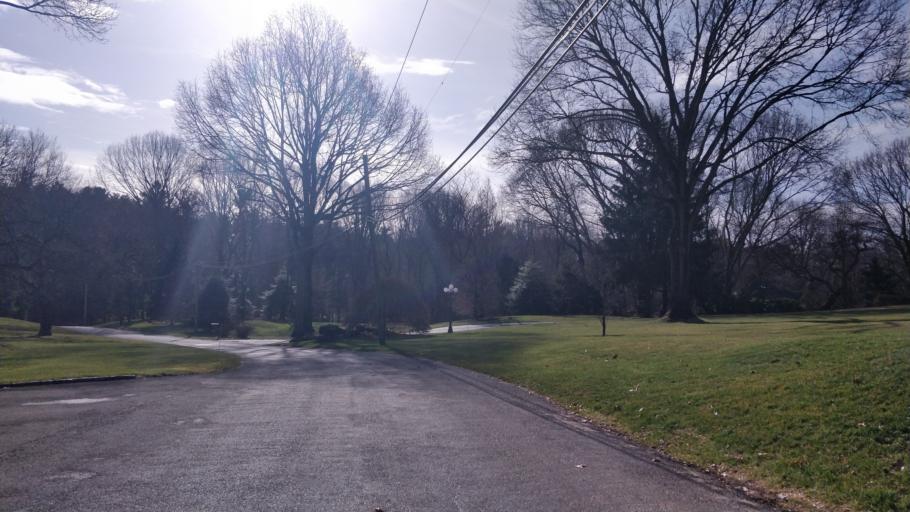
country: US
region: New York
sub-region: Nassau County
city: Oyster Bay
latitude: 40.8721
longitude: -73.5559
